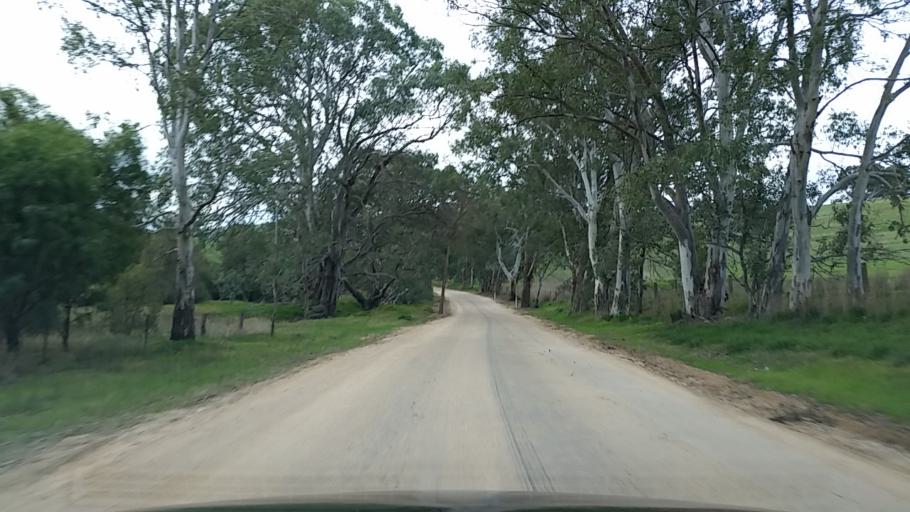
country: AU
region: South Australia
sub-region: Mount Barker
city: Nairne
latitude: -34.9559
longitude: 139.0110
